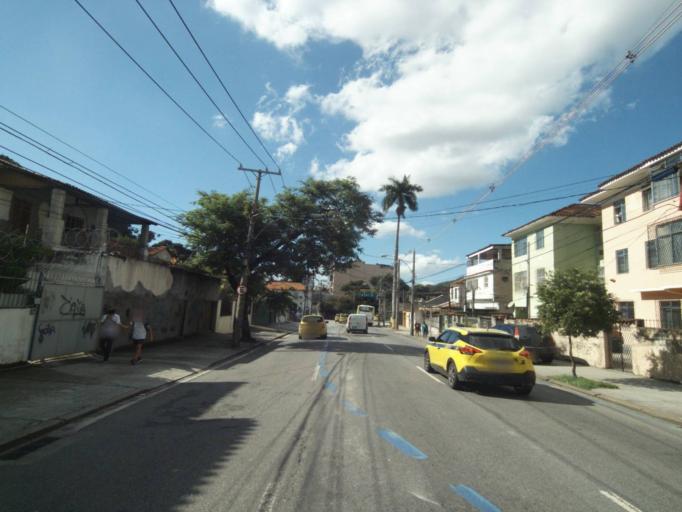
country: BR
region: Rio de Janeiro
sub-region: Rio De Janeiro
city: Rio de Janeiro
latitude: -22.9083
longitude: -43.2741
